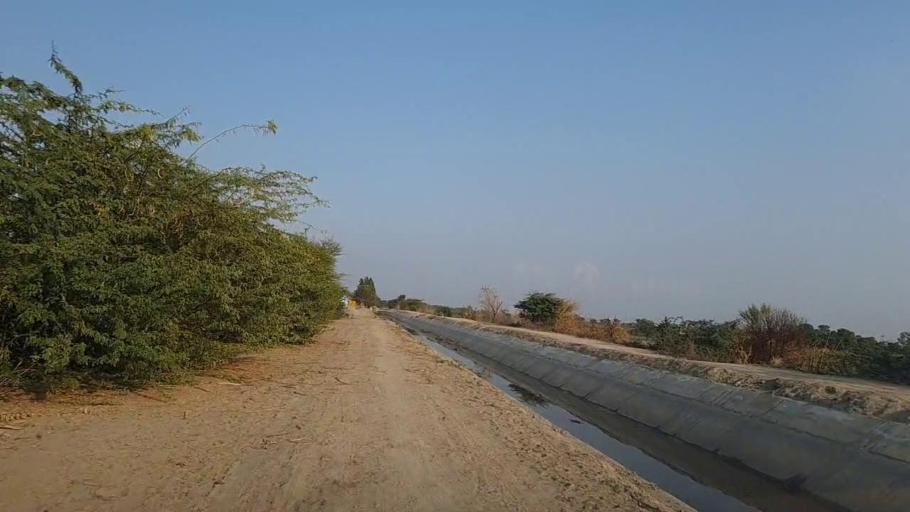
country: PK
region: Sindh
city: Jam Sahib
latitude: 26.3369
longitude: 68.5799
